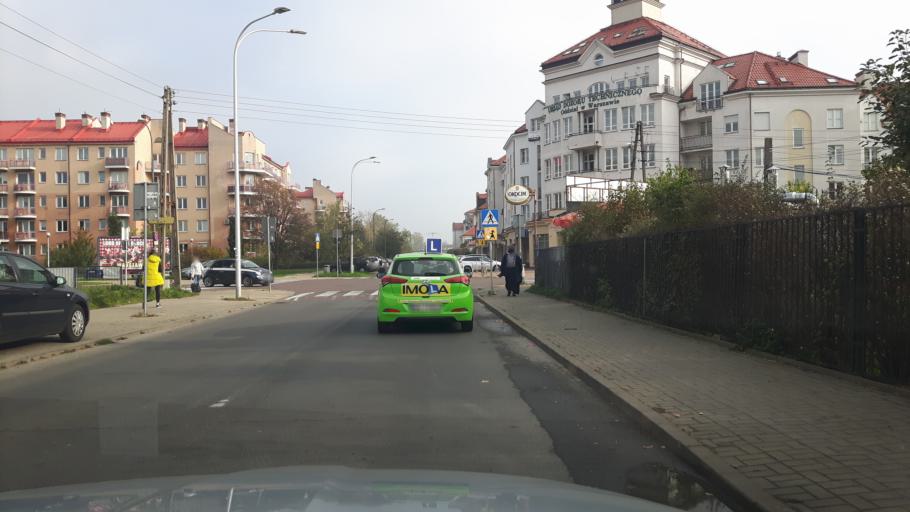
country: PL
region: Masovian Voivodeship
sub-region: Warszawa
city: Wlochy
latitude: 52.1918
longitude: 20.9660
